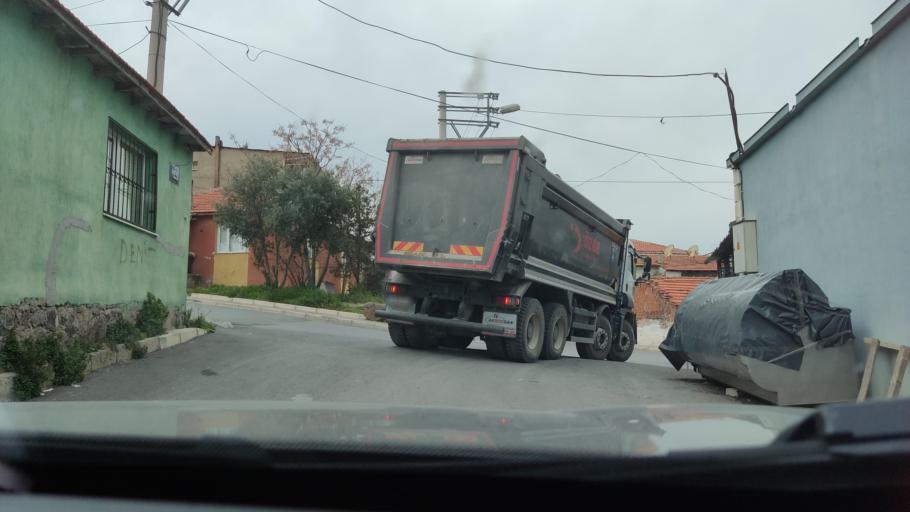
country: TR
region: Izmir
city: Karsiyaka
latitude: 38.5006
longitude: 27.0768
